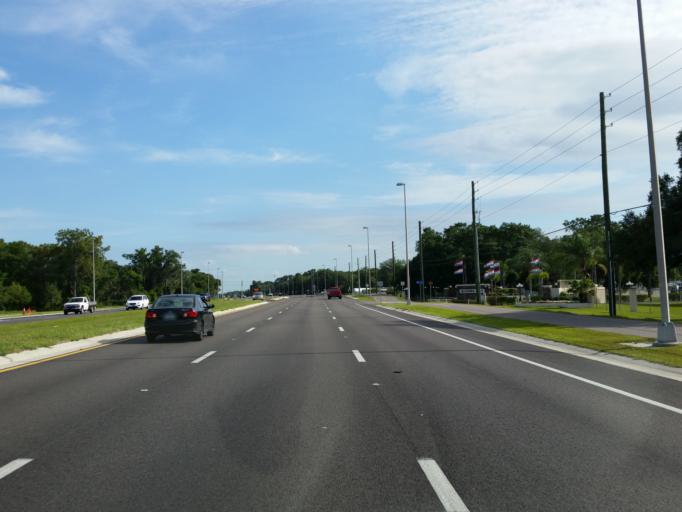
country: US
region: Florida
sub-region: Hillsborough County
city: Riverview
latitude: 27.8424
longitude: -82.3271
